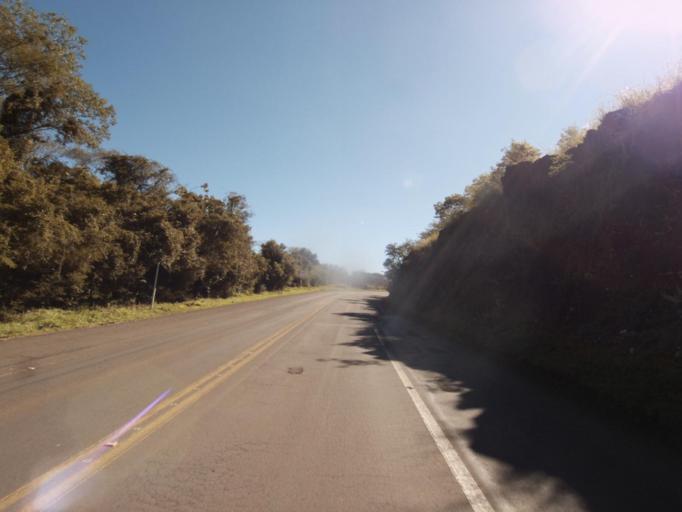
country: AR
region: Misiones
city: Bernardo de Irigoyen
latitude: -26.7855
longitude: -53.4592
